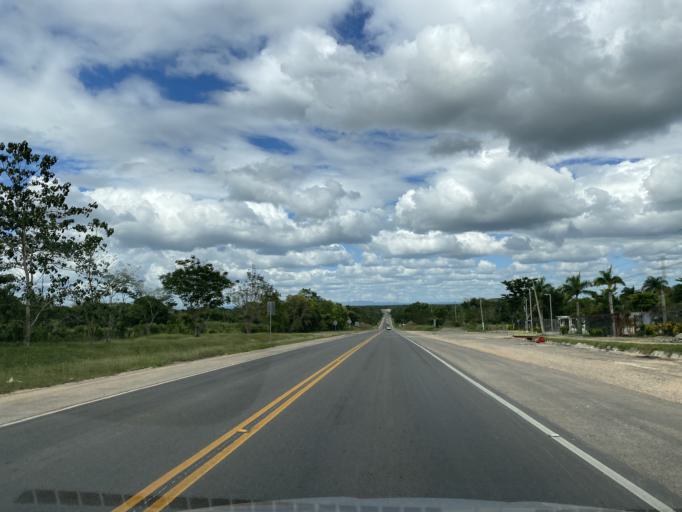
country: DO
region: Santo Domingo
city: Guerra
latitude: 18.5693
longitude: -69.7686
